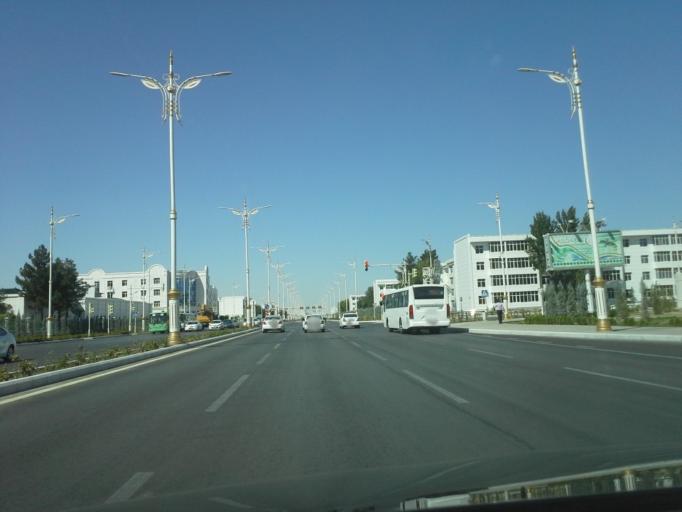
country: TM
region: Ahal
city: Ashgabat
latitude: 37.9574
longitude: 58.3765
